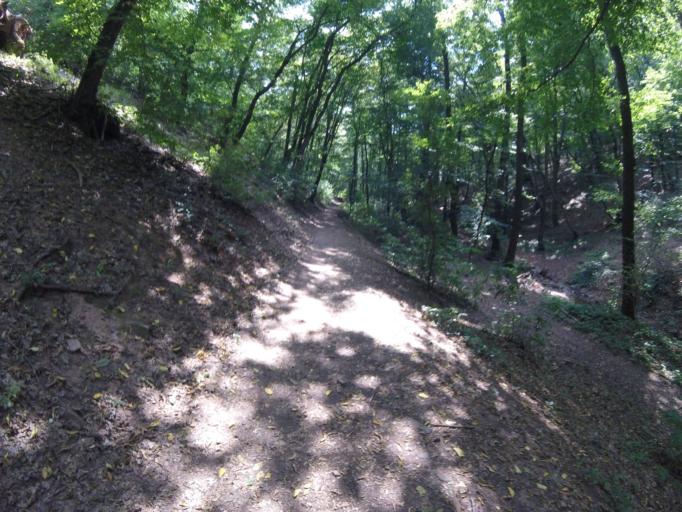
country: HU
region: Baranya
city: Pecs
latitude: 46.0913
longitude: 18.1778
